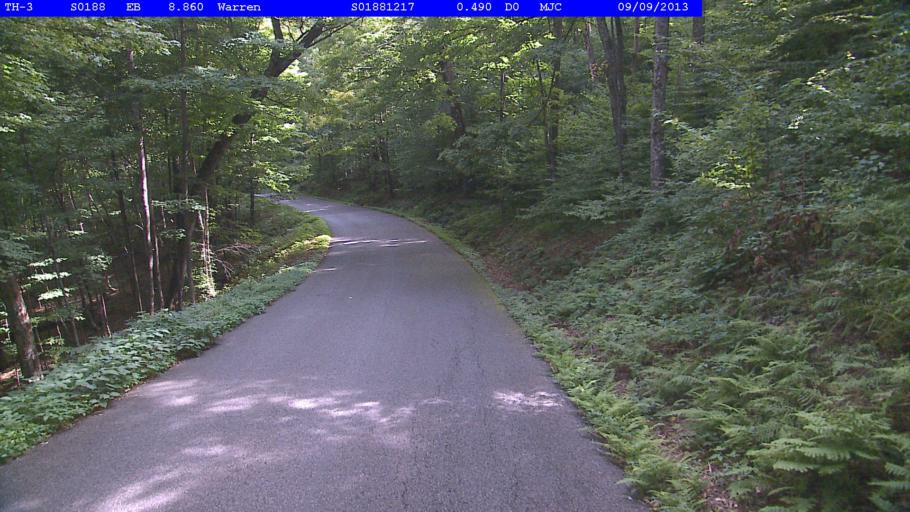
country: US
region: Vermont
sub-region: Addison County
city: Bristol
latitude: 44.0927
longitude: -72.9144
